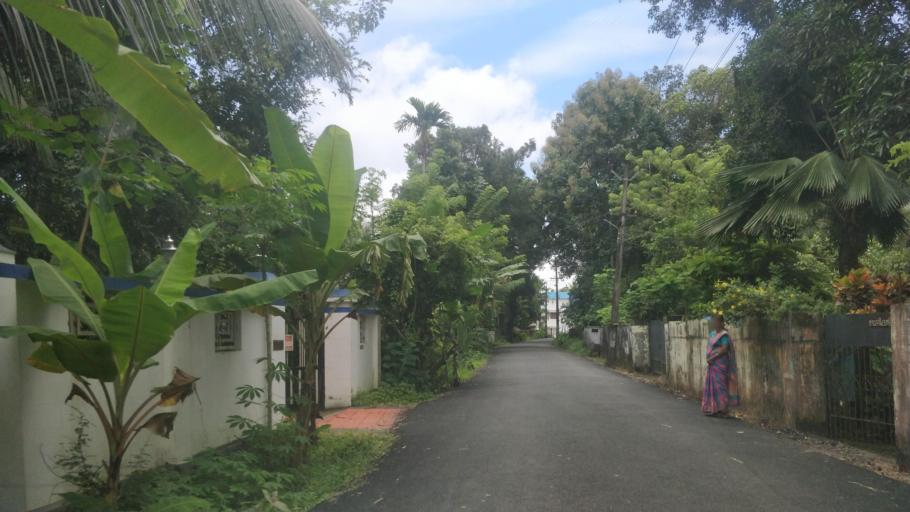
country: IN
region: Kerala
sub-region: Alappuzha
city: Shertallai
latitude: 9.6624
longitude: 76.3749
